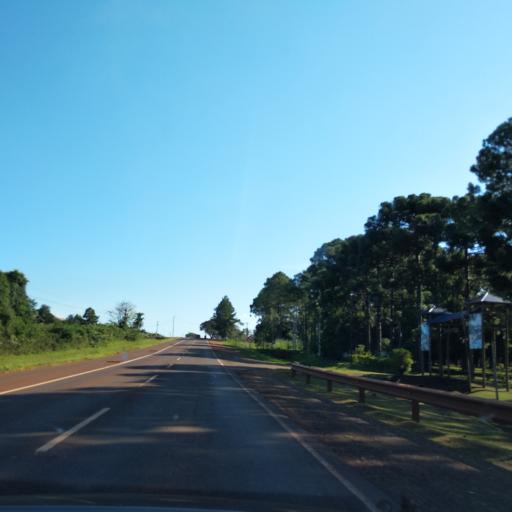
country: AR
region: Misiones
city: Jardin America
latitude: -27.0583
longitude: -55.2571
